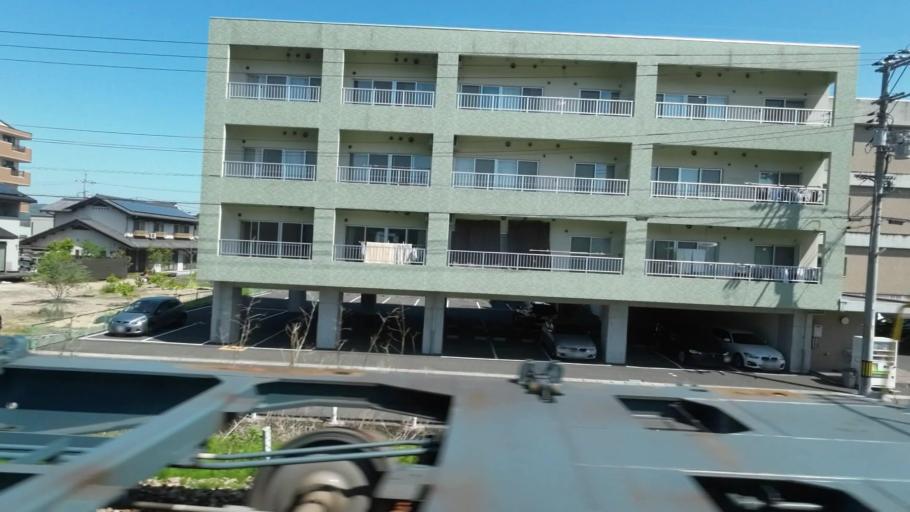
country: JP
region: Hiroshima
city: Onomichi
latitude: 34.4374
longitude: 133.2350
